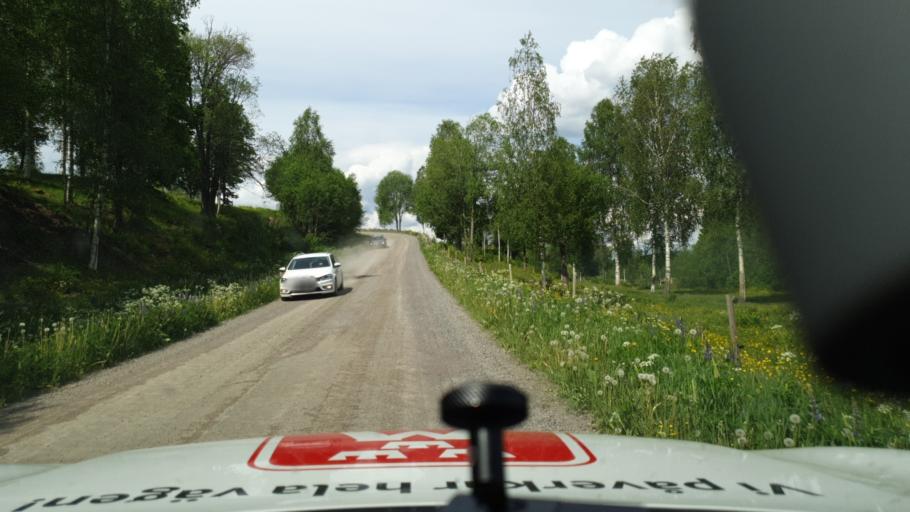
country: SE
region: Vaermland
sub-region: Torsby Kommun
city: Torsby
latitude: 59.9471
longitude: 12.9008
